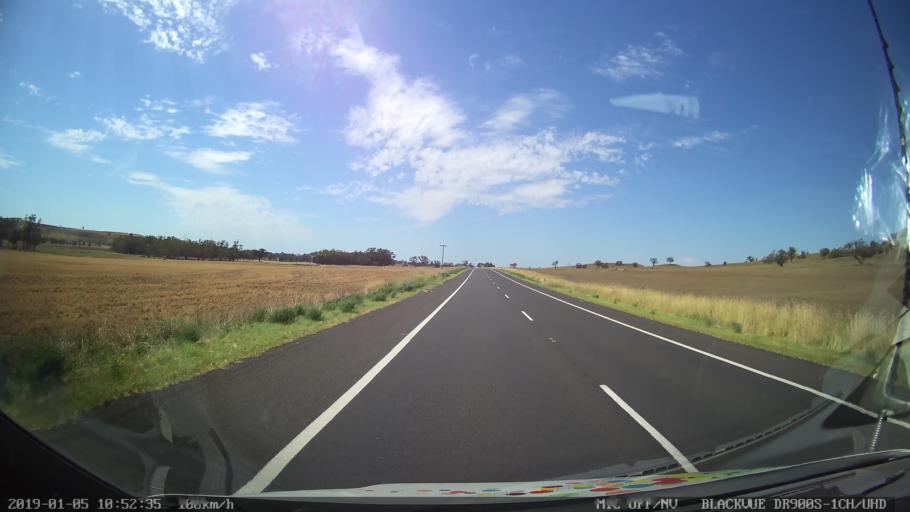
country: AU
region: New South Wales
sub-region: Warrumbungle Shire
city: Coonabarabran
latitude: -31.4333
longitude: 149.1048
